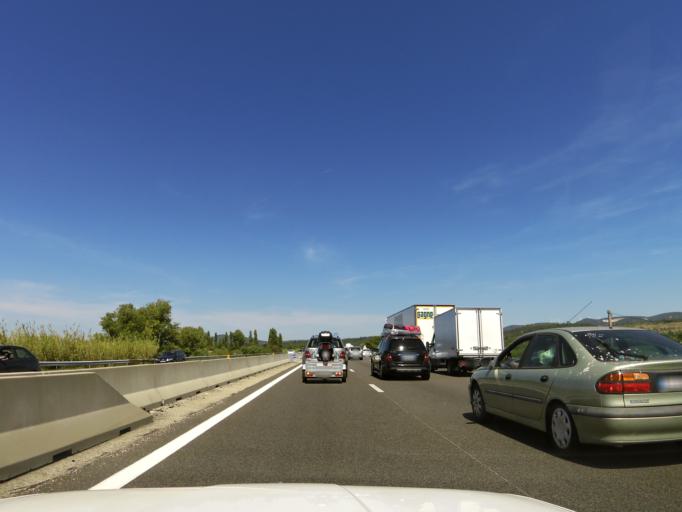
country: FR
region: Rhone-Alpes
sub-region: Departement de la Drome
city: La Garde-Adhemar
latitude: 44.4088
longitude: 4.7298
